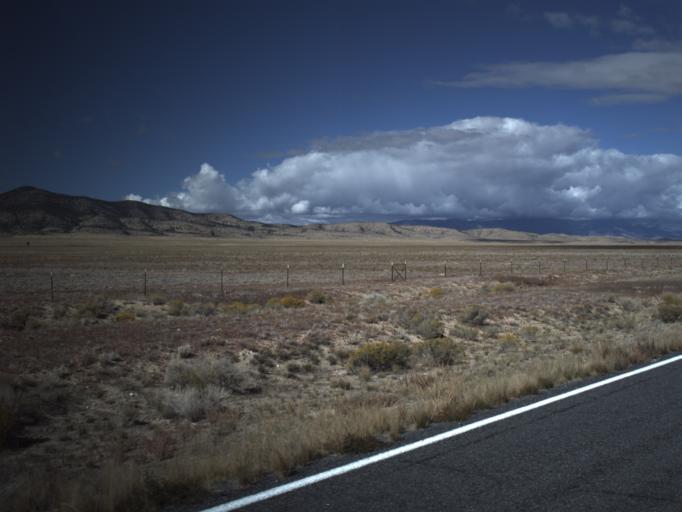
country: US
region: Utah
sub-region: Beaver County
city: Milford
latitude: 38.6488
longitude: -113.8678
